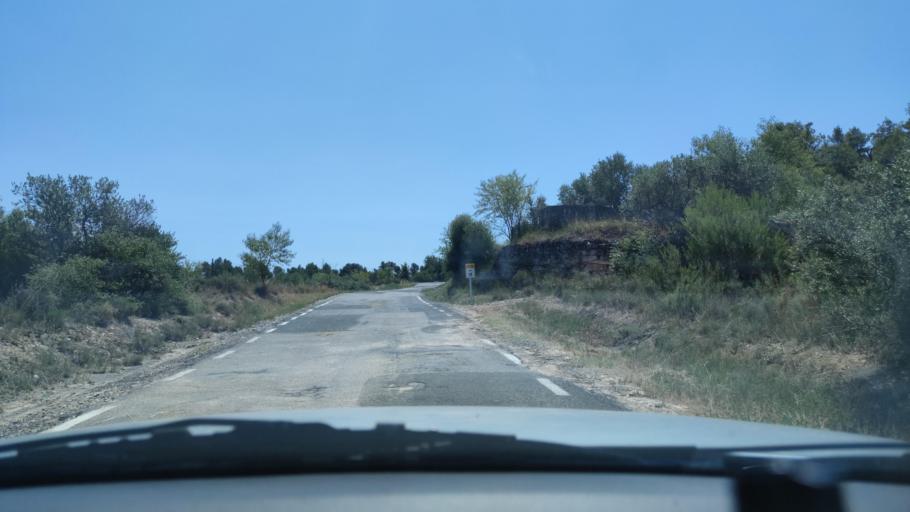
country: ES
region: Catalonia
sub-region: Provincia de Lleida
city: Fulleda
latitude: 41.4797
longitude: 1.0175
